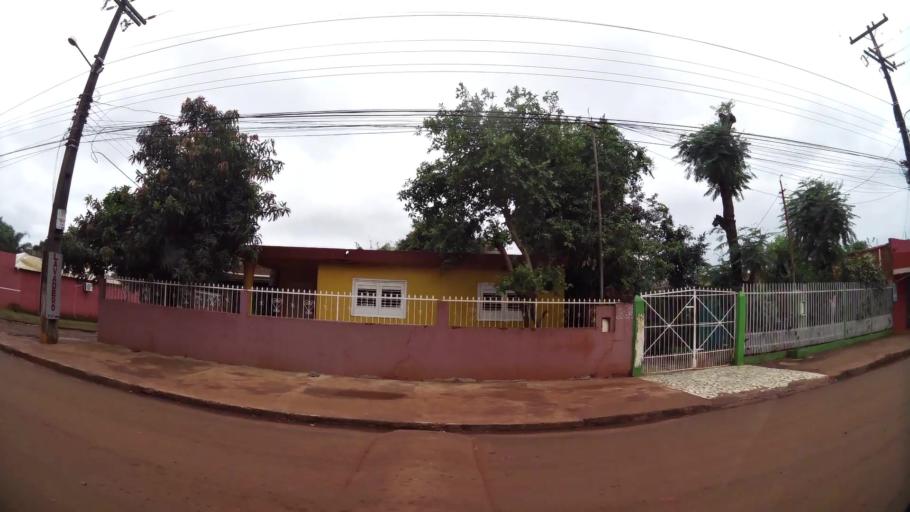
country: PY
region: Alto Parana
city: Presidente Franco
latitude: -25.5045
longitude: -54.6881
